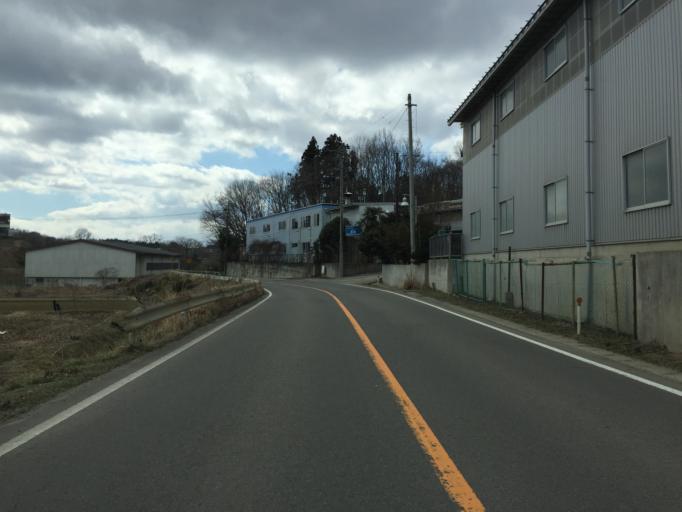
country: JP
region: Fukushima
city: Fukushima-shi
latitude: 37.6632
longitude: 140.5136
